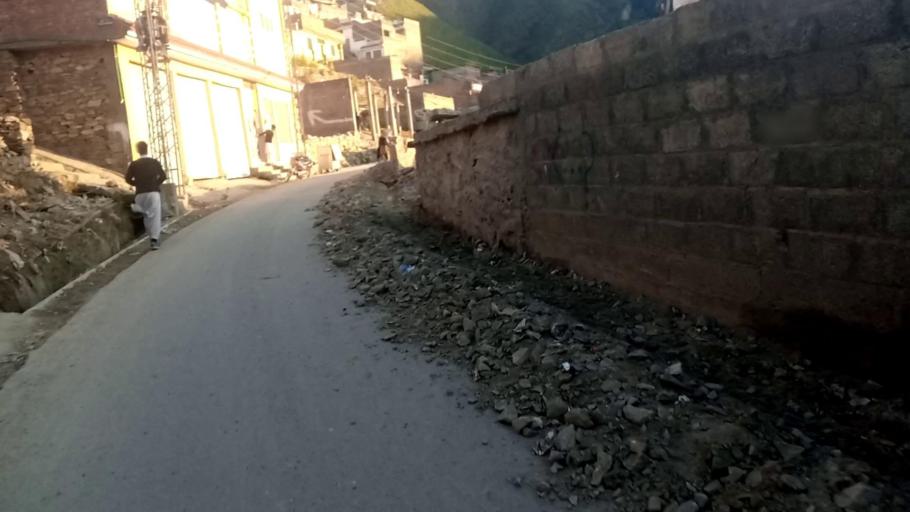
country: PK
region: Khyber Pakhtunkhwa
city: Saidu Sharif
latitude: 34.7384
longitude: 72.3447
